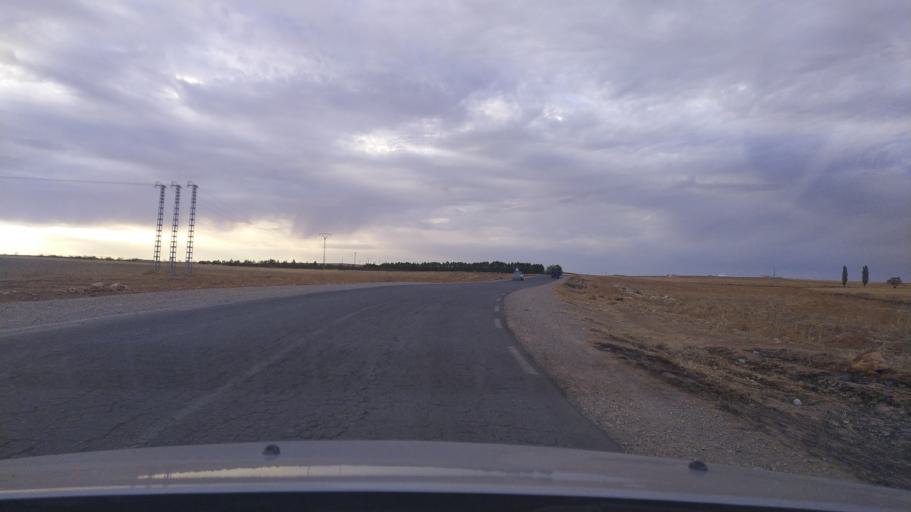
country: DZ
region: Tiaret
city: Frenda
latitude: 34.9820
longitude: 1.1453
